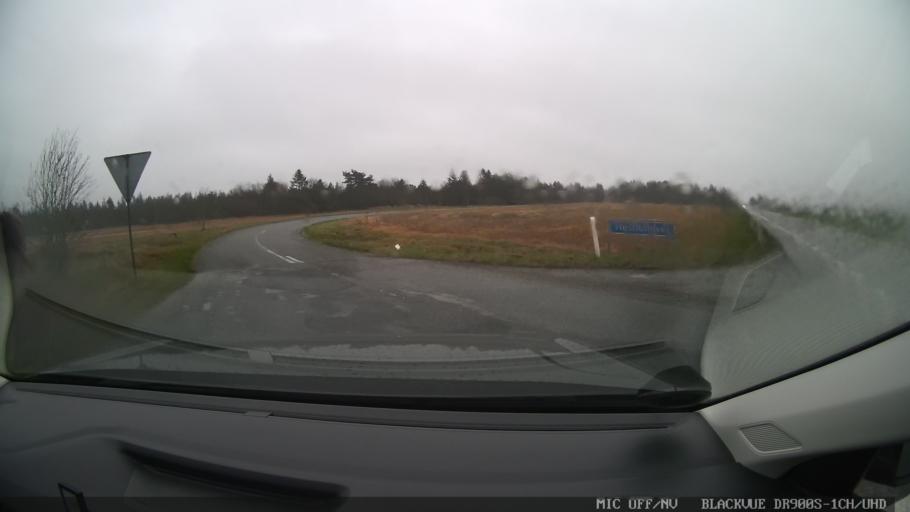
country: DK
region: Central Jutland
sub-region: Herning Kommune
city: Sunds
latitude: 56.2364
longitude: 9.0996
